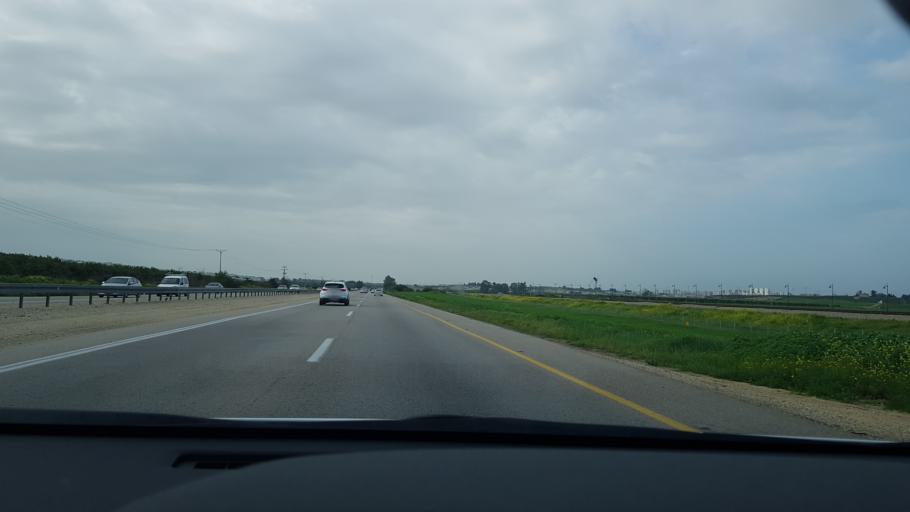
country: IL
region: Southern District
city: Ashqelon
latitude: 31.7140
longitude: 34.6282
